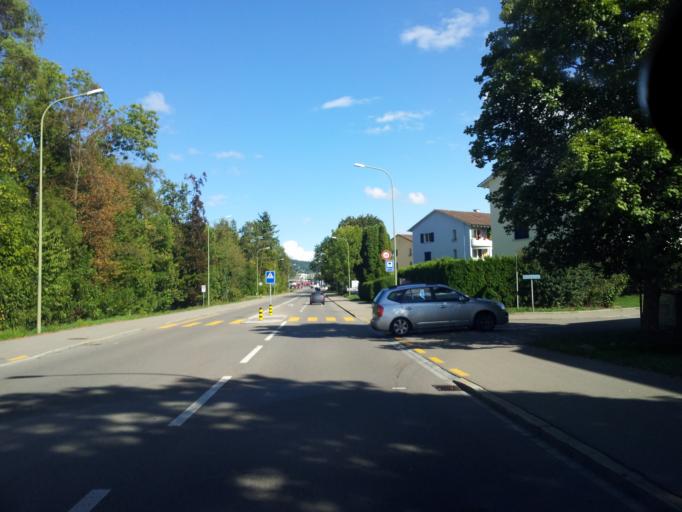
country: CH
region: Zurich
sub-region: Bezirk Dietikon
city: Dietikon / Vorstadt
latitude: 47.4093
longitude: 8.3937
